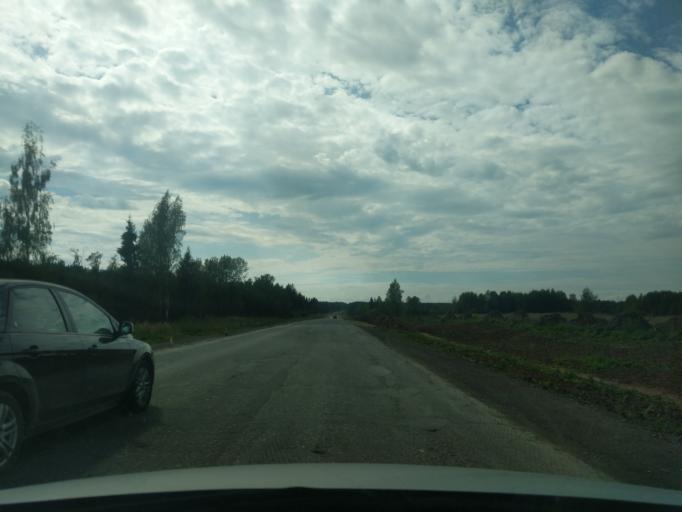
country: RU
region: Kostroma
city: Sudislavl'
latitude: 57.8576
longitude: 41.6091
